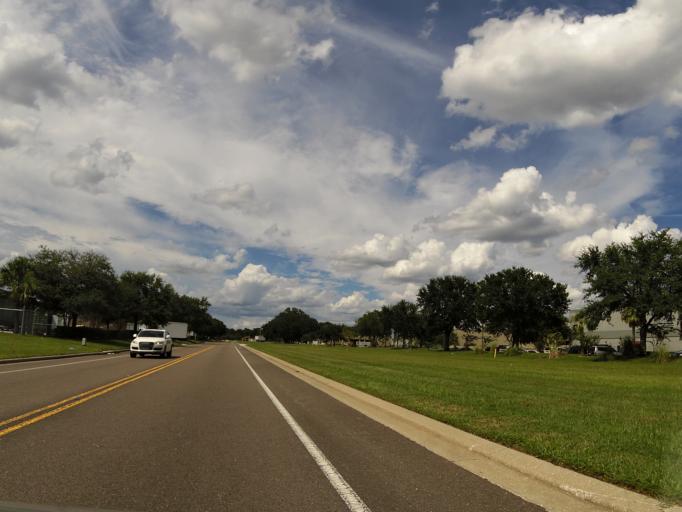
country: US
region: Florida
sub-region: Duval County
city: Jacksonville
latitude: 30.4228
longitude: -81.6358
